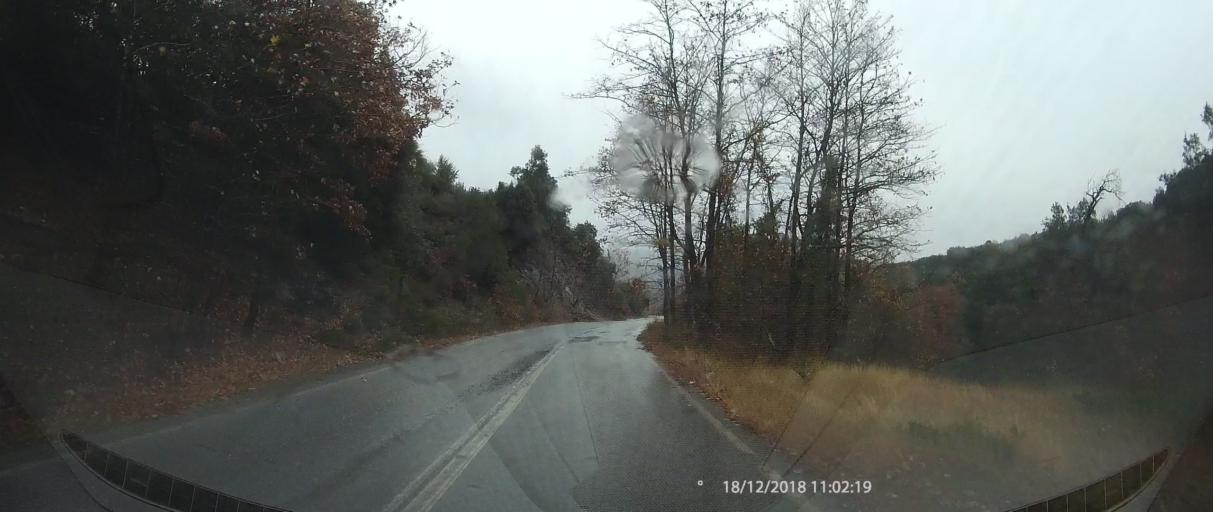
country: GR
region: Central Macedonia
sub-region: Nomos Pierias
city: Kato Milia
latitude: 40.2031
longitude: 22.3172
